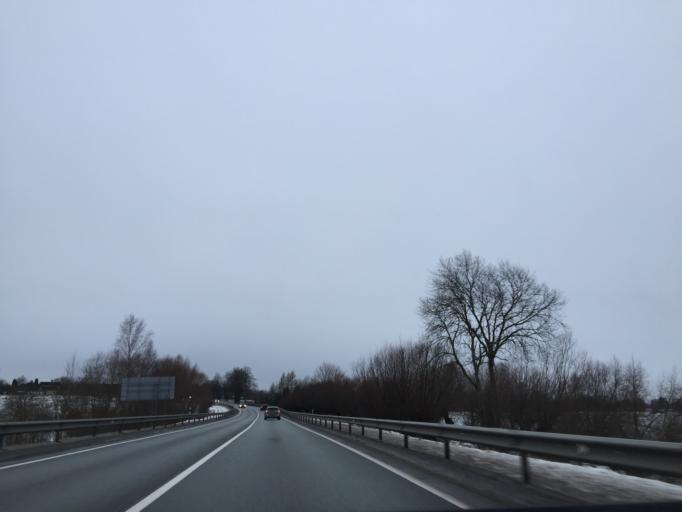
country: LV
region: Krimulda
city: Ragana
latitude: 57.1770
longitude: 24.7108
